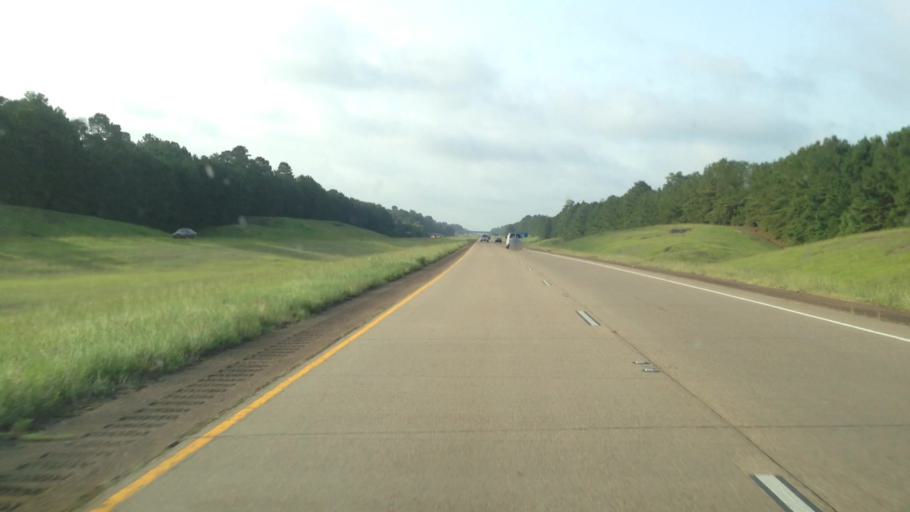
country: US
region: Louisiana
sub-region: Rapides Parish
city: Lecompte
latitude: 31.0881
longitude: -92.4429
